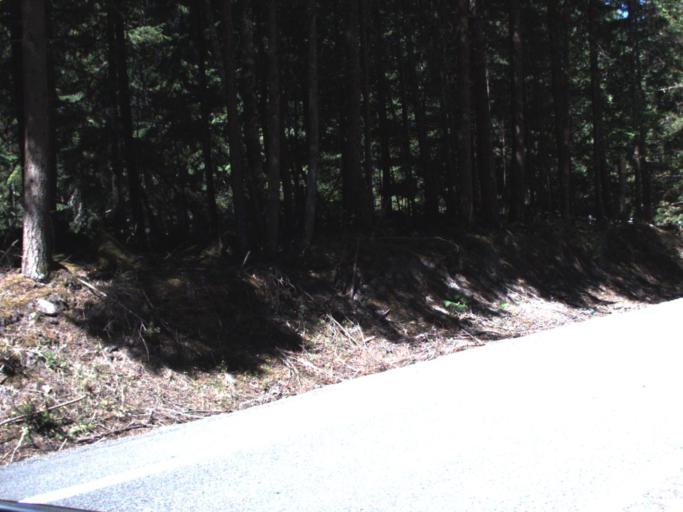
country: US
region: Washington
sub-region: King County
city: Riverbend
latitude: 47.1107
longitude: -121.5998
